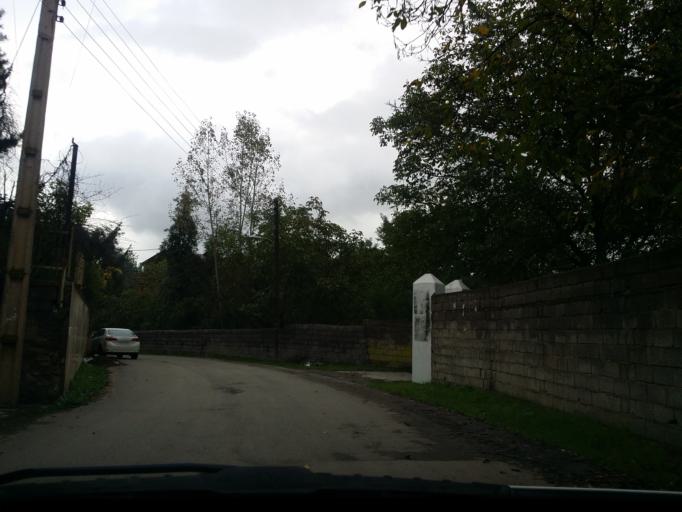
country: IR
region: Mazandaran
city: `Abbasabad
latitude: 36.5071
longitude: 51.1901
